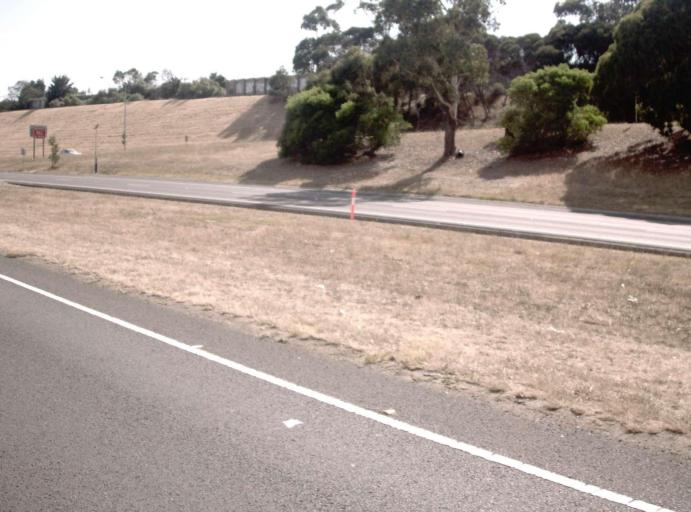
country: AU
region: Victoria
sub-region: Casey
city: Eumemmerring
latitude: -38.0032
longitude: 145.2519
